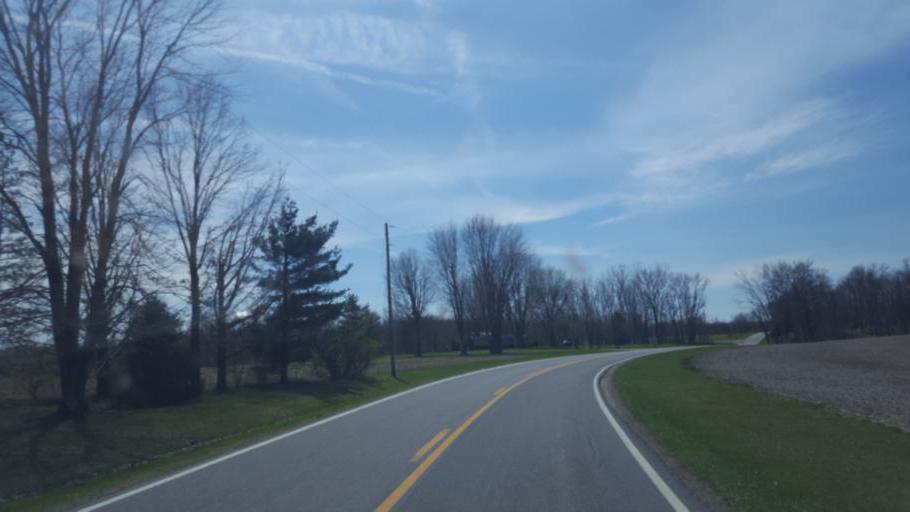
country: US
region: Ohio
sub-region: Delaware County
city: Ashley
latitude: 40.4015
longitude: -83.0303
